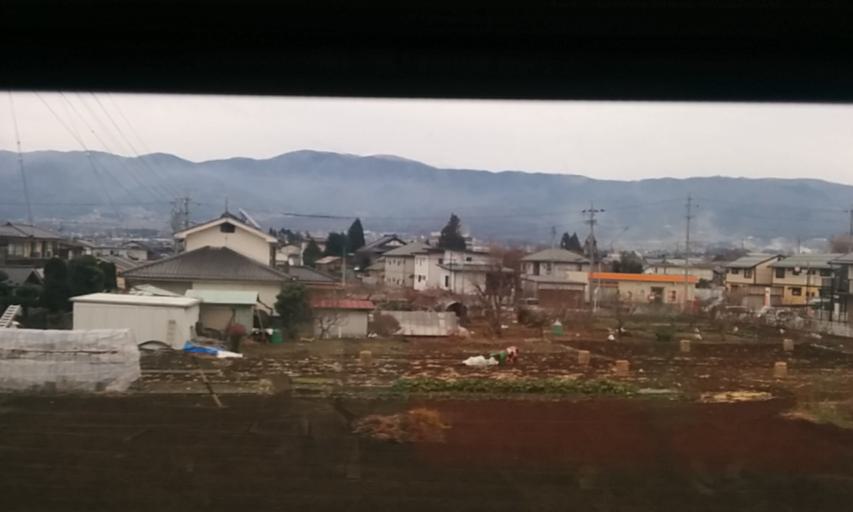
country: JP
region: Nagano
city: Matsumoto
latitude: 36.1772
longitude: 137.9575
